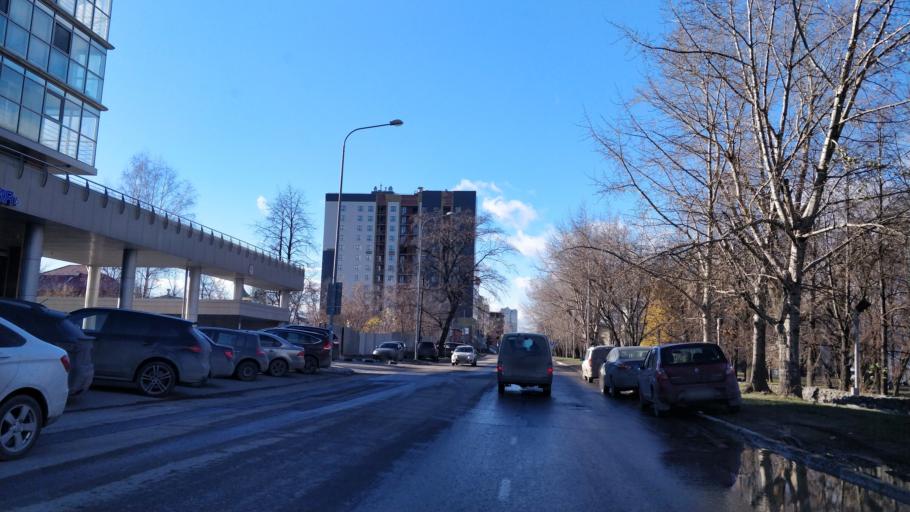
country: RU
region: Perm
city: Perm
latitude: 58.0149
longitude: 56.2224
